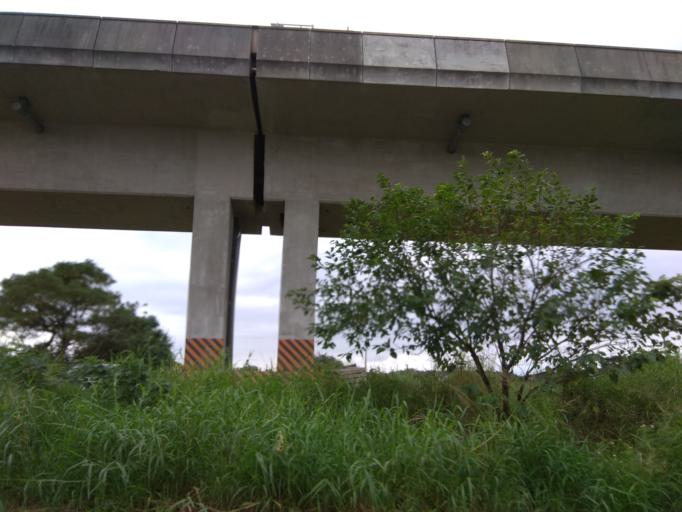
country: TW
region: Taiwan
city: Taoyuan City
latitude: 25.0439
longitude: 121.2153
